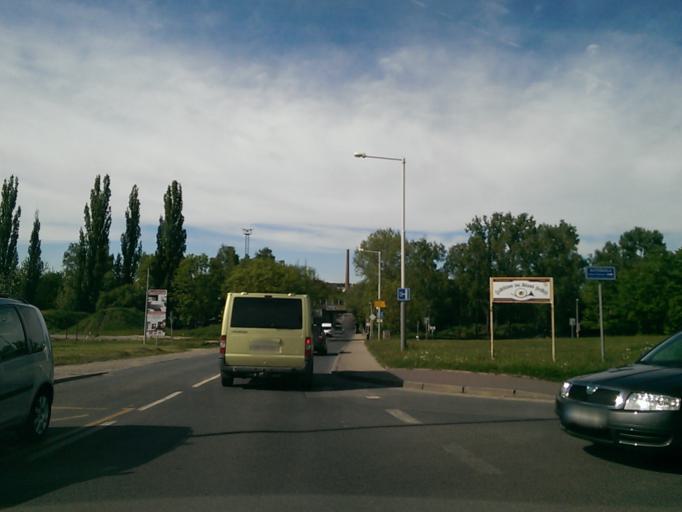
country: CZ
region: Praha
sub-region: Praha 20
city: Horni Pocernice
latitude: 50.0817
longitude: 14.6164
